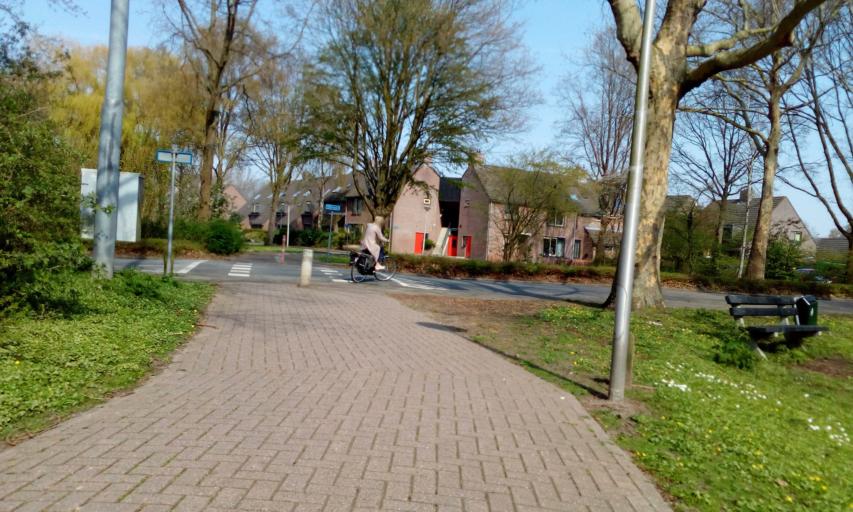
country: NL
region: South Holland
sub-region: Gemeente Spijkenisse
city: Spijkenisse
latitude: 51.8362
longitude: 4.3429
